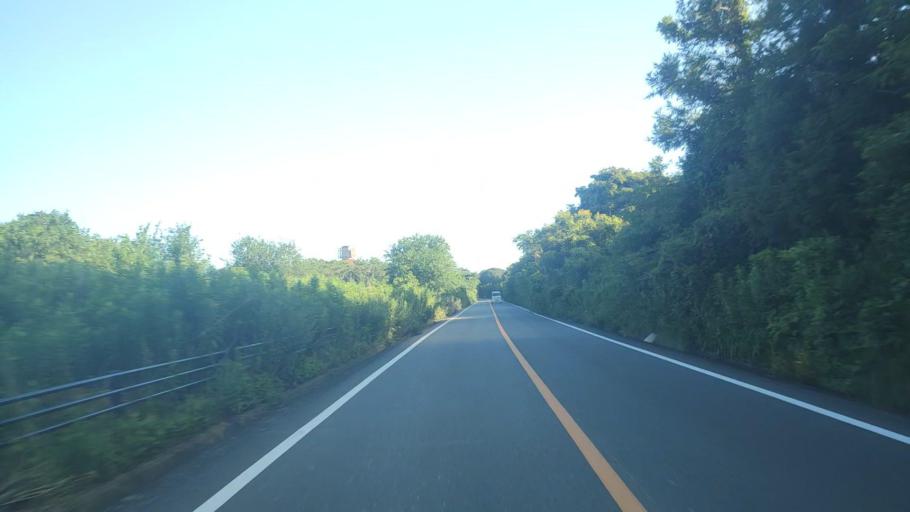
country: JP
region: Mie
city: Toba
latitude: 34.3399
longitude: 136.8399
